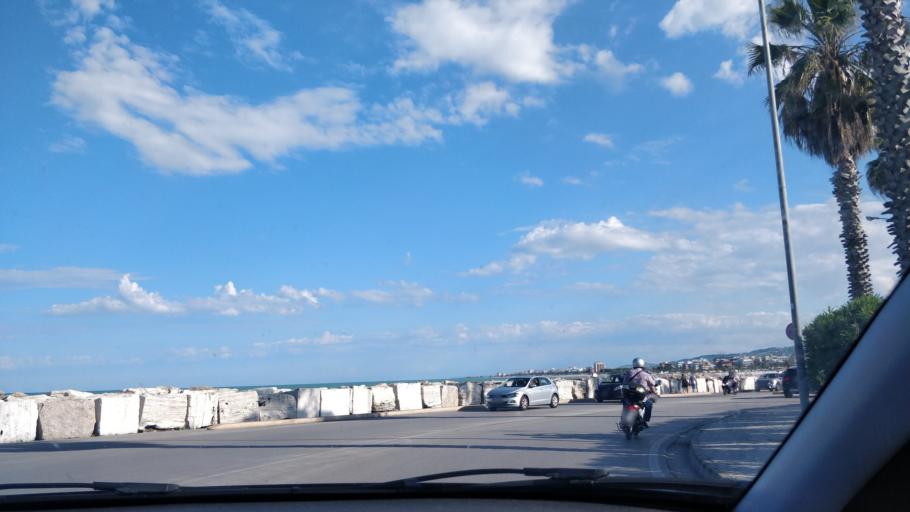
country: IT
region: The Marches
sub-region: Provincia di Ascoli Piceno
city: Grottammare
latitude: 42.9520
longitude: 13.8889
